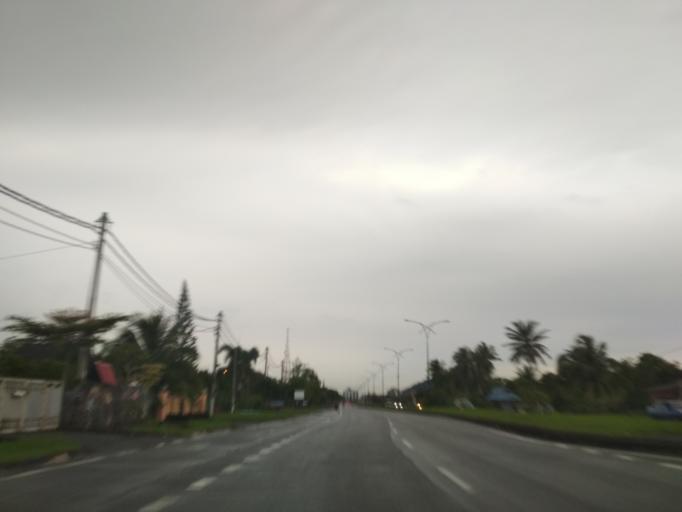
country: MY
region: Perlis
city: Kangar
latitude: 6.4609
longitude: 100.2085
